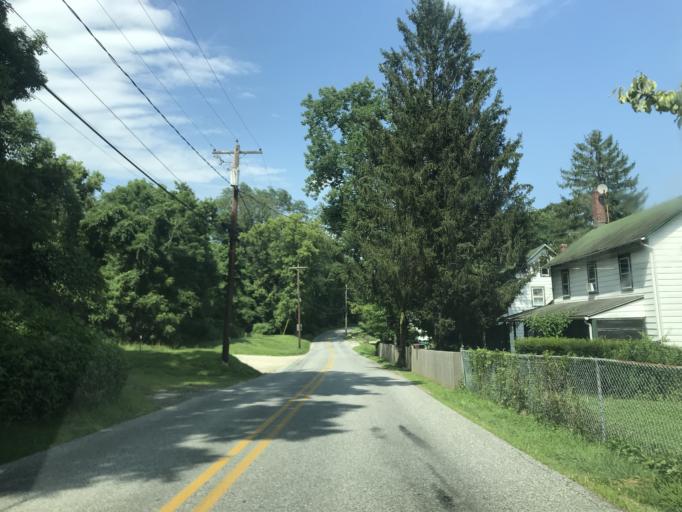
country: US
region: Delaware
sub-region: New Castle County
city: Greenville
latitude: 39.8328
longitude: -75.5850
